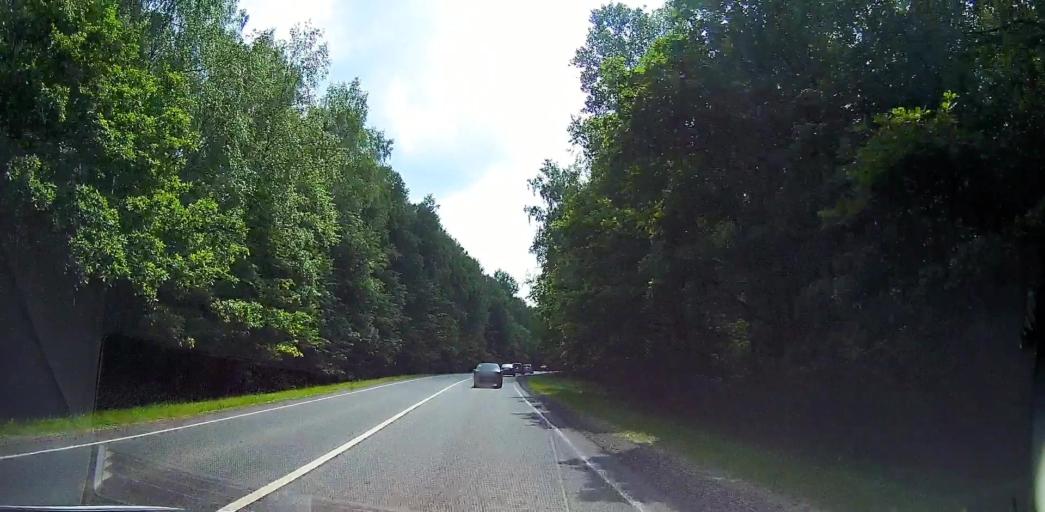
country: RU
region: Moskovskaya
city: Stupino
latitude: 54.9828
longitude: 38.1675
